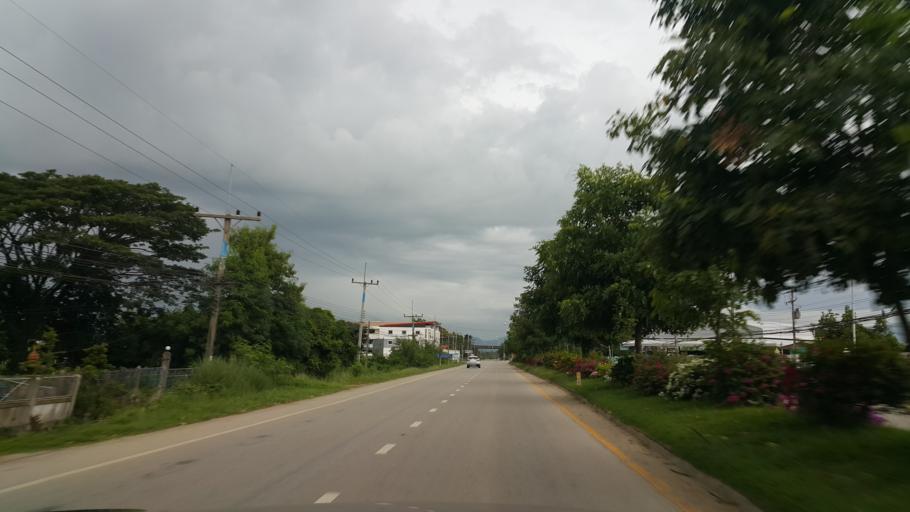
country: TH
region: Phayao
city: Dok Kham Tai
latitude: 19.1708
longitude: 100.0053
